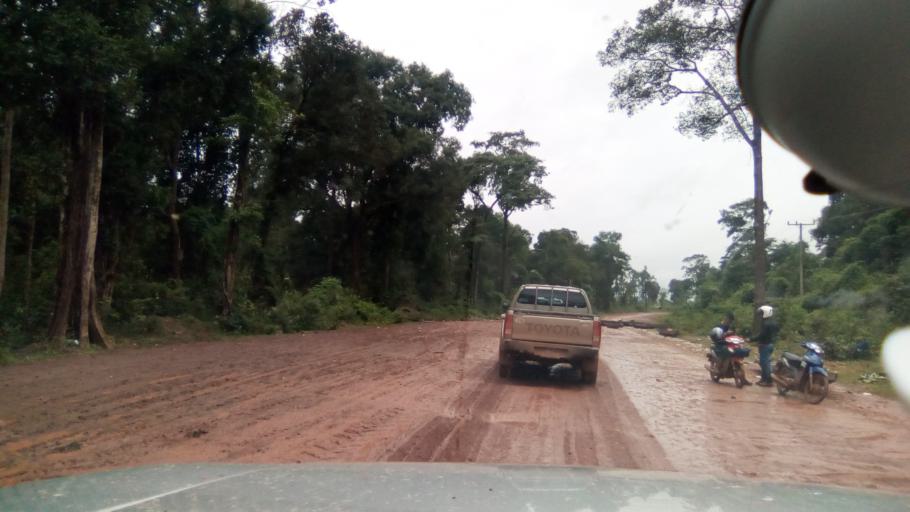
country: LA
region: Attapu
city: Attapu
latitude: 14.6838
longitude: 106.5523
